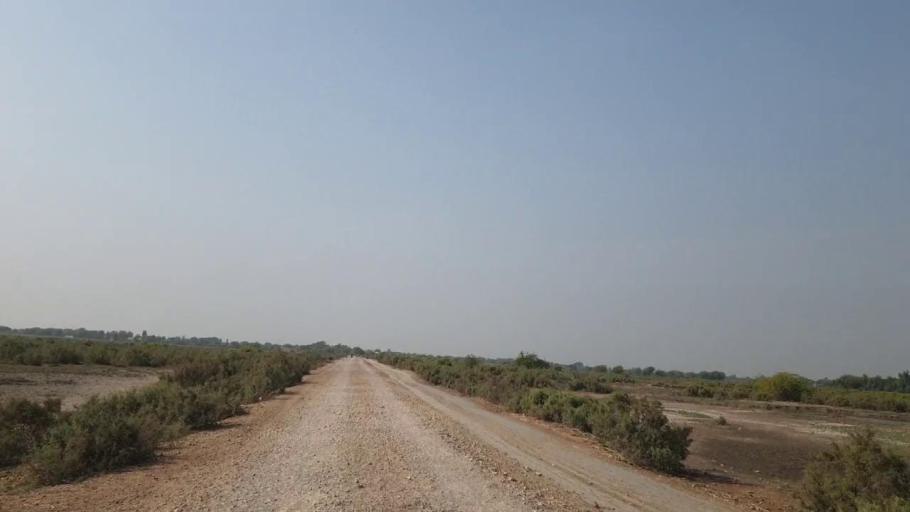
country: PK
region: Sindh
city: Kario
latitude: 24.9390
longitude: 68.5463
